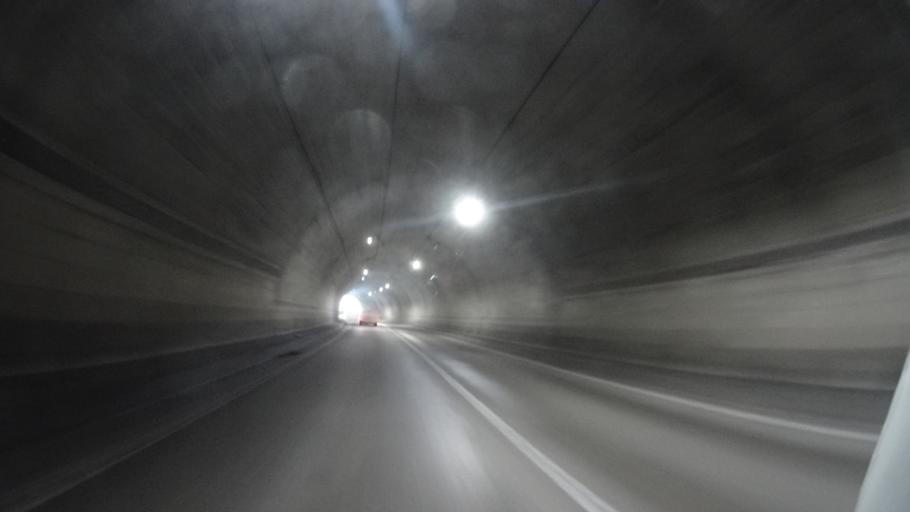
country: JP
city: Asahi
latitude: 35.9570
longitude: 136.0144
